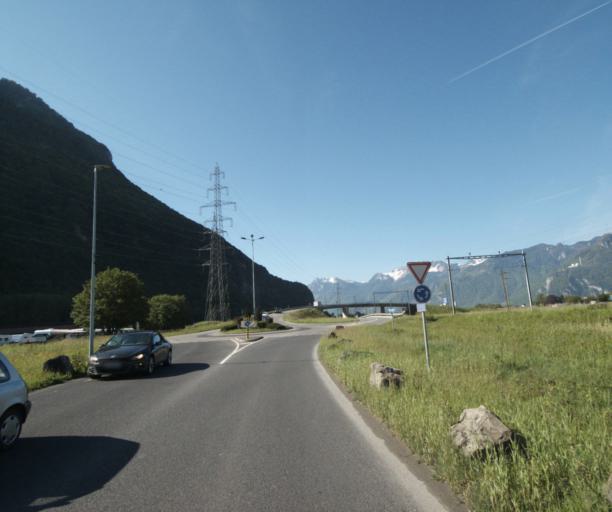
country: CH
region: Vaud
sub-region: Aigle District
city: Villeneuve
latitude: 46.3798
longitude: 6.9286
